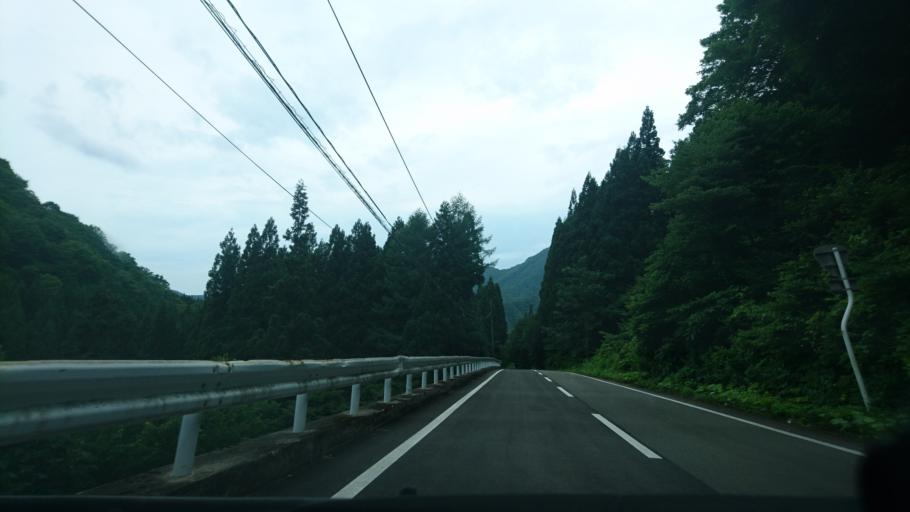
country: JP
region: Akita
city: Yuzawa
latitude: 39.1697
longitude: 140.7364
